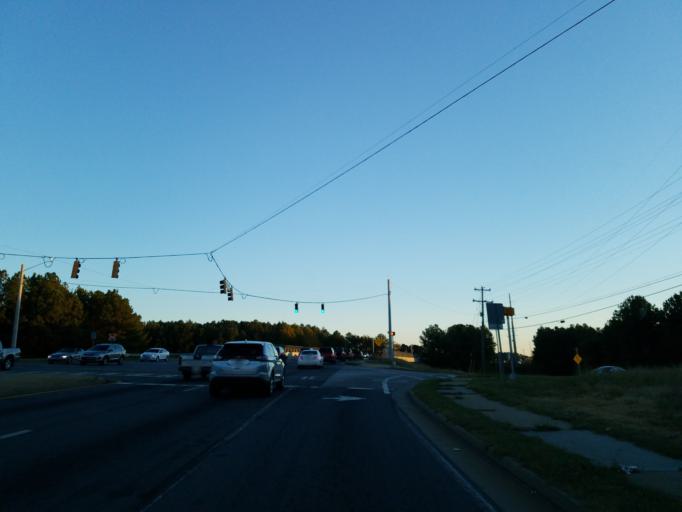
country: US
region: Georgia
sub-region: Forsyth County
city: Cumming
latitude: 34.1594
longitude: -84.1734
